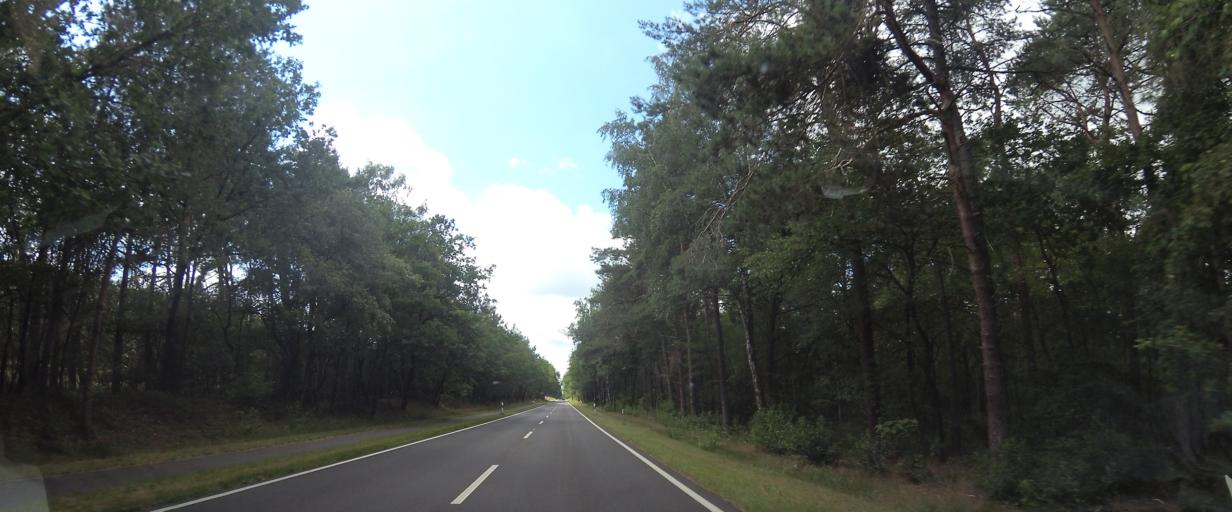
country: DE
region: Lower Saxony
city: Niederlangen
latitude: 52.8098
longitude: 7.3149
